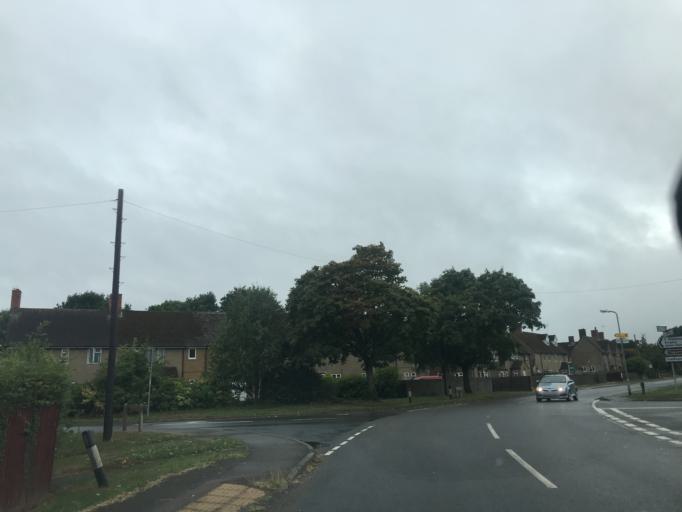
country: GB
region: England
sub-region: Buckinghamshire
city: Haddenham
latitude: 51.7730
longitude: -0.9187
